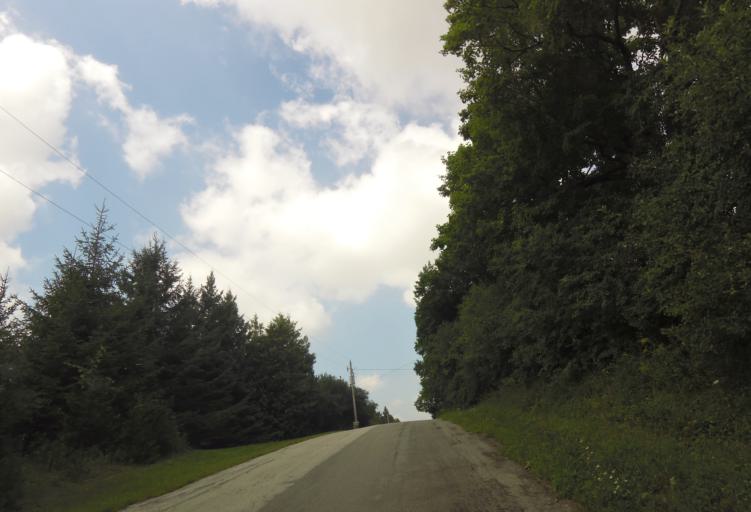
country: CA
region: Ontario
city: Oshawa
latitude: 43.9936
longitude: -78.8733
